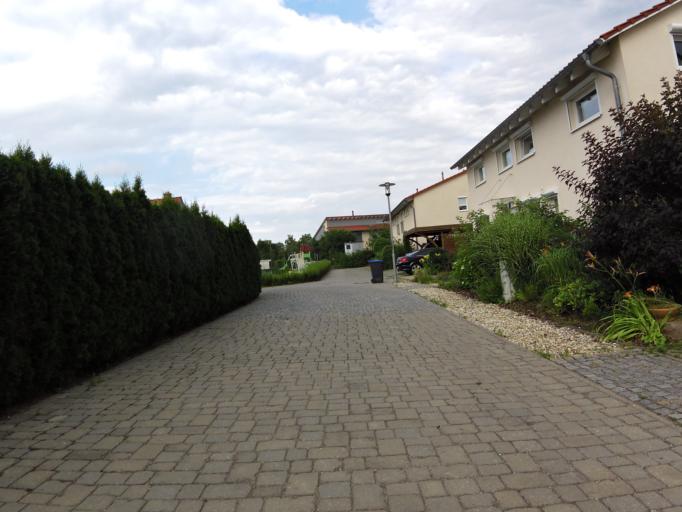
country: DE
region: Saxony
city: Zwenkau
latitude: 51.2685
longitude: 12.2915
